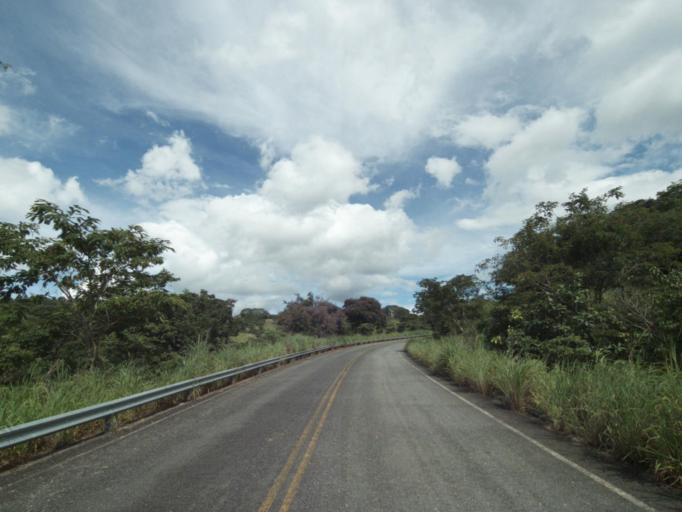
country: BR
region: Goias
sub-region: Pirenopolis
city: Pirenopolis
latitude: -15.7779
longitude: -49.0508
